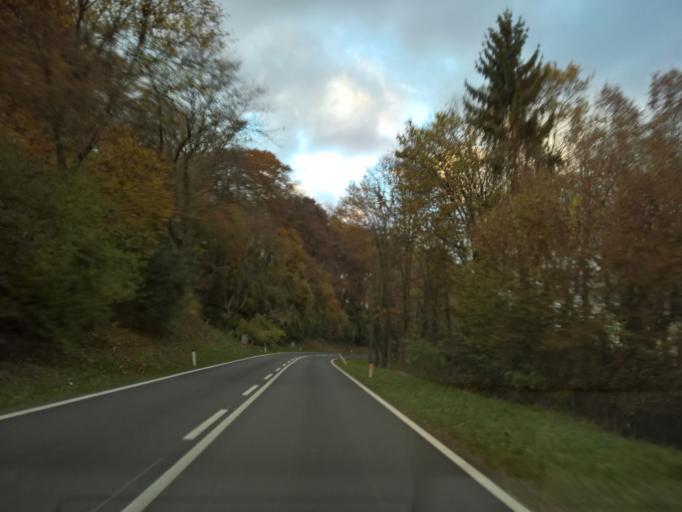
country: AT
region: Styria
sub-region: Politischer Bezirk Leibnitz
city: Stocking
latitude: 46.8769
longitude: 15.5274
